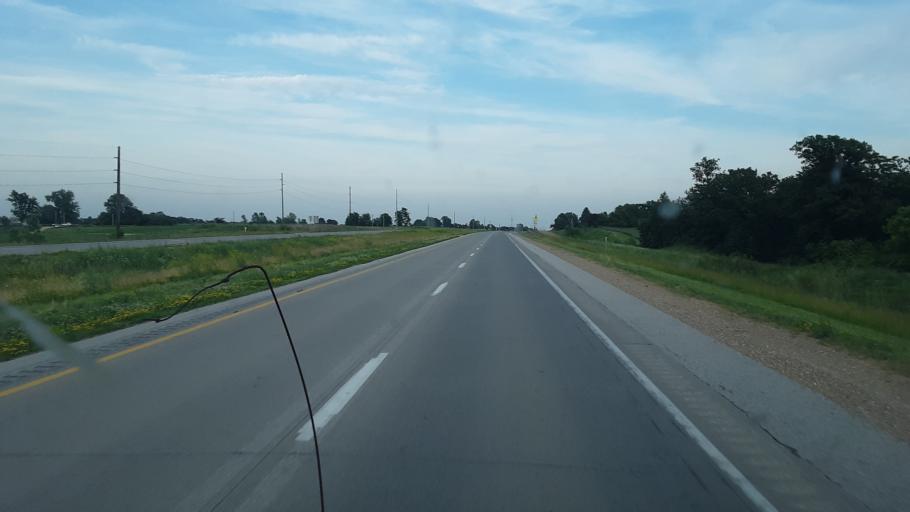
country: US
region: Iowa
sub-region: Tama County
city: Toledo
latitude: 41.9977
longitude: -92.6457
